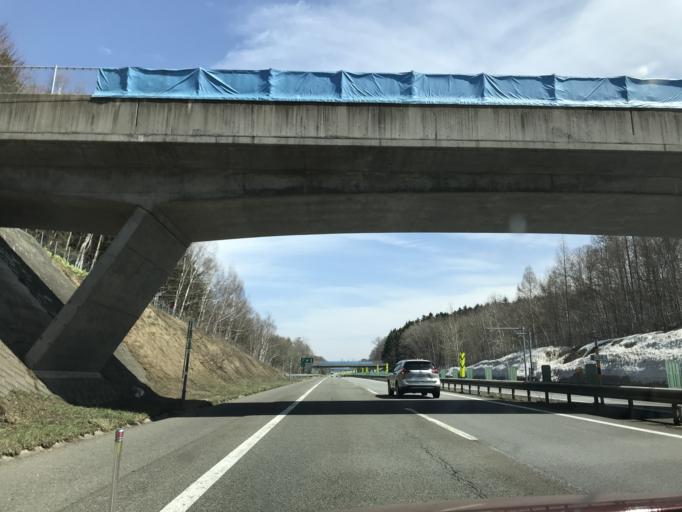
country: JP
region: Hokkaido
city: Iwamizawa
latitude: 43.1865
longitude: 141.7874
